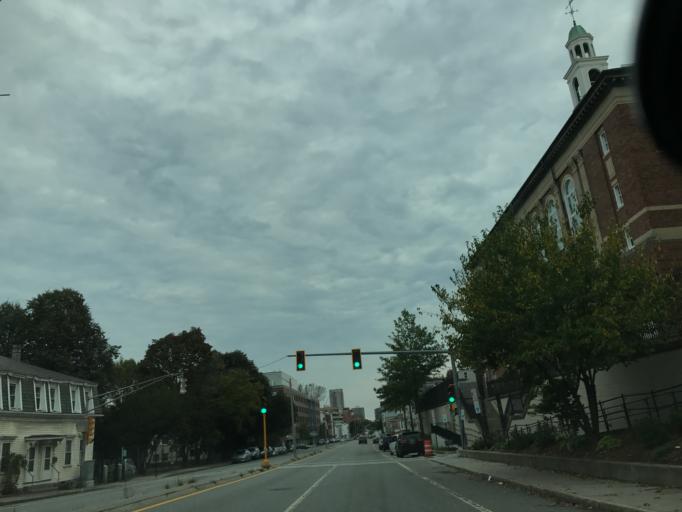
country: US
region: Massachusetts
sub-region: Norfolk County
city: Brookline
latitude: 42.3305
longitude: -71.1229
